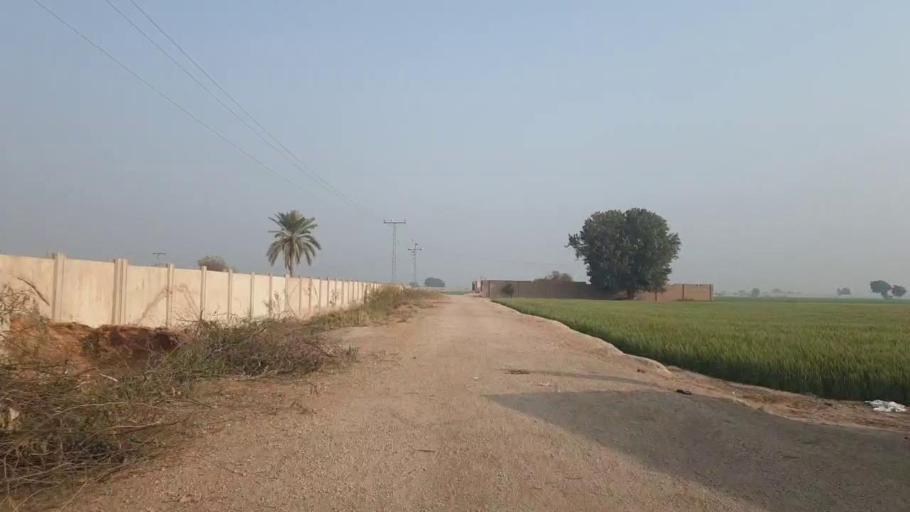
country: PK
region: Sindh
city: Hala
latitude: 25.8047
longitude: 68.4078
